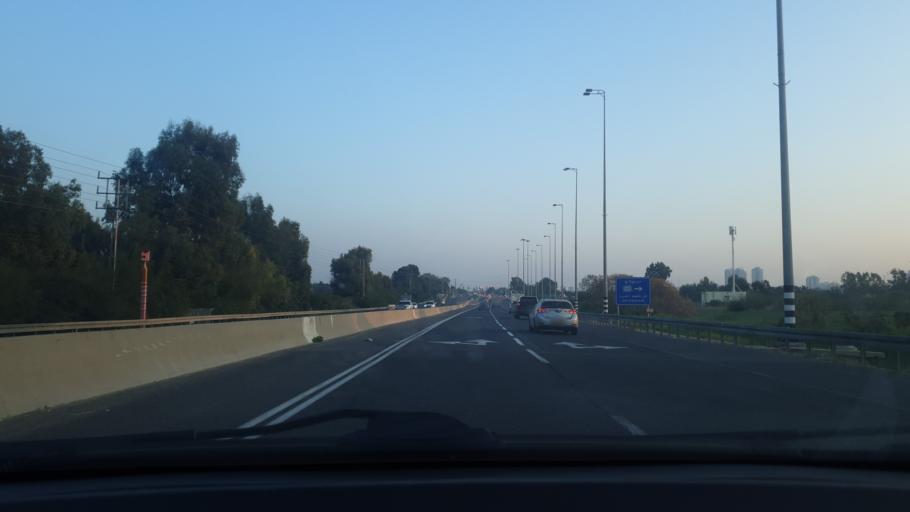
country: IL
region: Central District
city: Ramla
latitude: 31.9555
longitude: 34.8545
